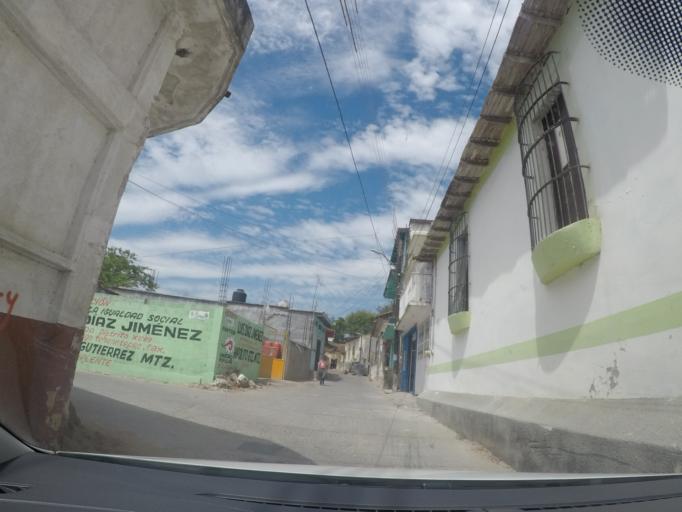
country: MX
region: Oaxaca
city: San Blas Atempa
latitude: 16.3333
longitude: -95.2303
